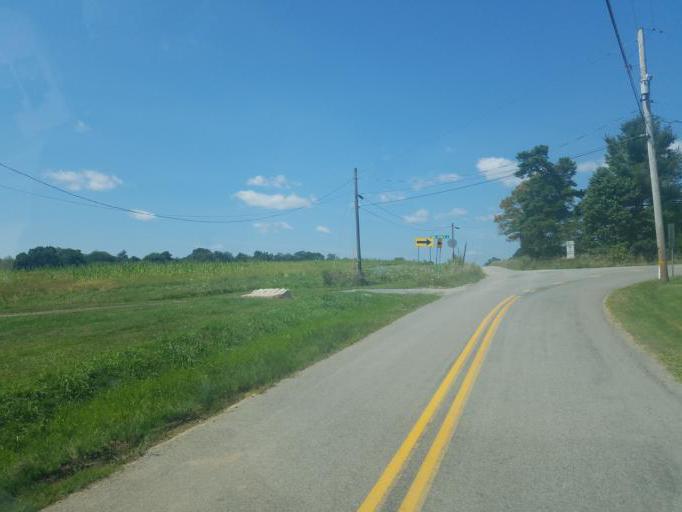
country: US
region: Pennsylvania
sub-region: Clarion County
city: Knox
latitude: 41.2003
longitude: -79.5560
